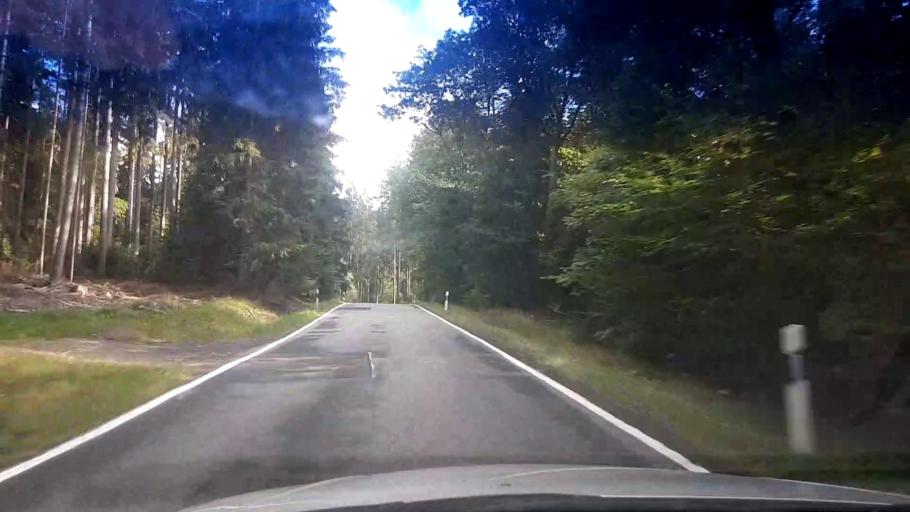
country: DE
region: Bavaria
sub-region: Upper Palatinate
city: Neualbenreuth
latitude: 49.9458
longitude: 12.4187
